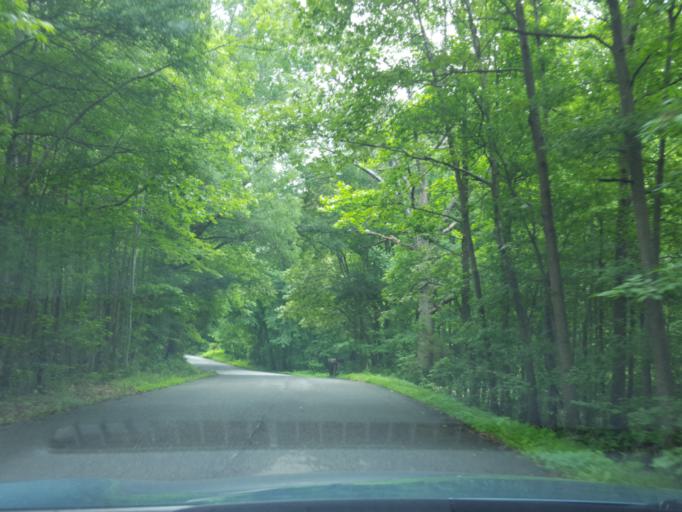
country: US
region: Maryland
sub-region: Calvert County
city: Dunkirk
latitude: 38.7762
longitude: -76.6841
